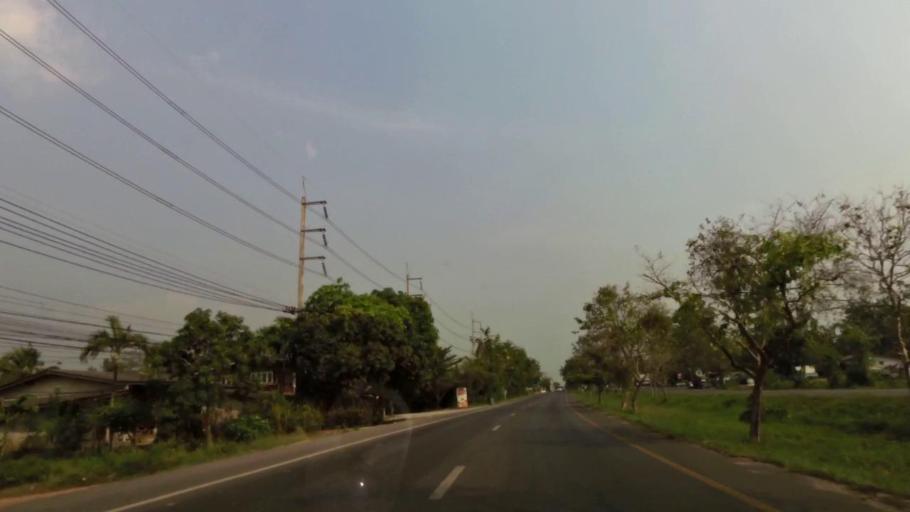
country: TH
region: Rayong
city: Klaeng
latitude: 12.7854
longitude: 101.6815
